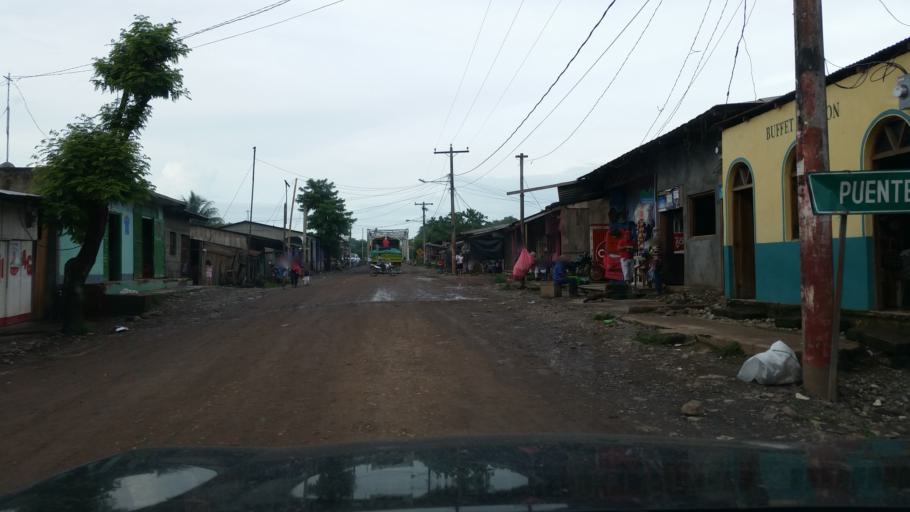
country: NI
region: Matagalpa
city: Rio Blanco
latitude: 13.1717
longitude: -84.9600
